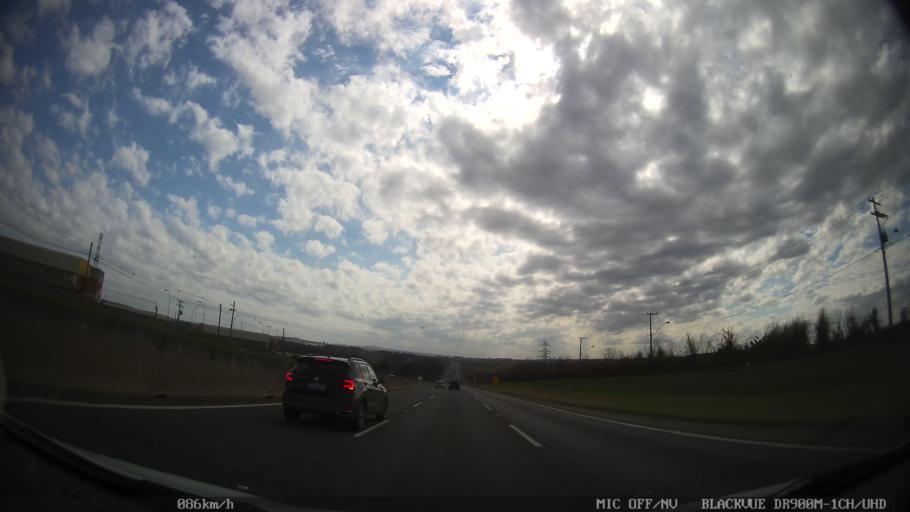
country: BR
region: Sao Paulo
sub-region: Limeira
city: Limeira
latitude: -22.6257
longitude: -47.3418
